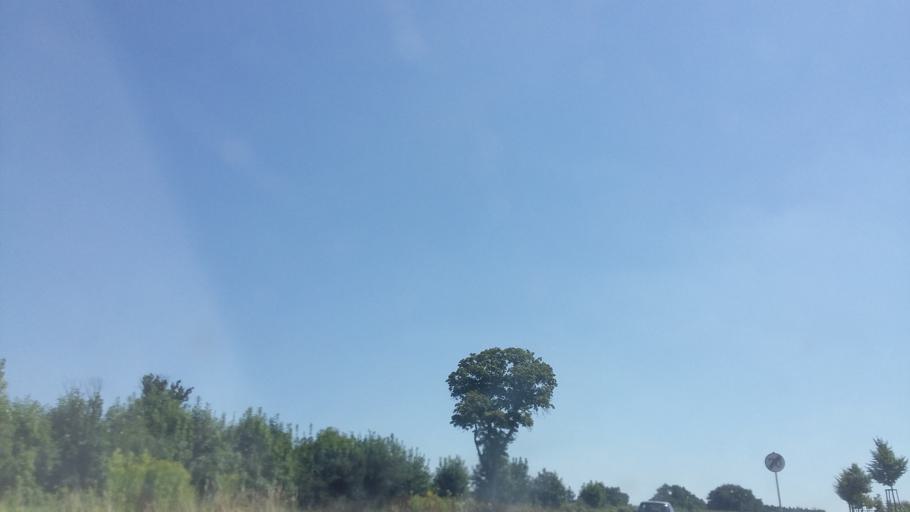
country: DE
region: Bavaria
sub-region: Upper Bavaria
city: Emmering
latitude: 48.1656
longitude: 11.2780
